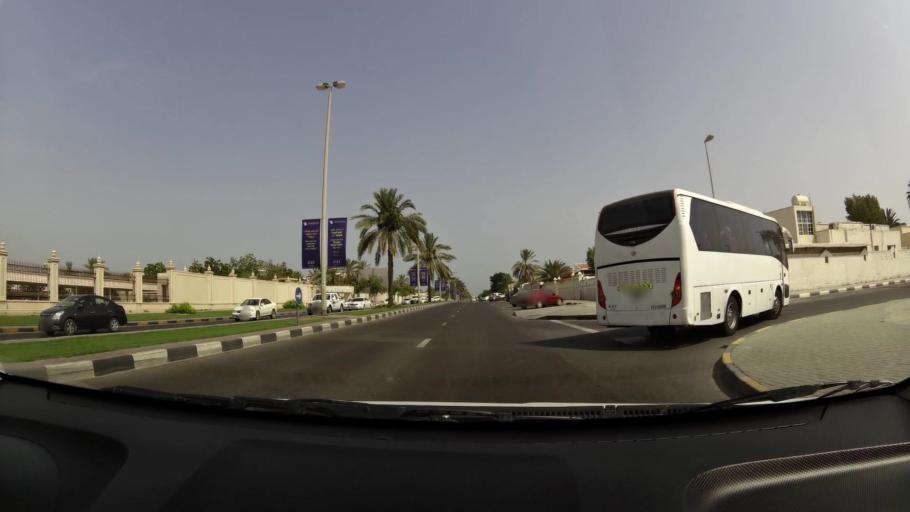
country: AE
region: Ash Shariqah
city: Sharjah
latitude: 25.3577
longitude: 55.4262
